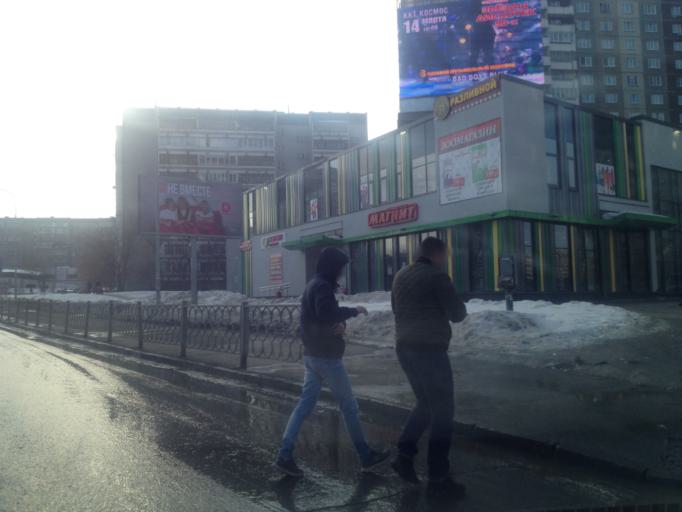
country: RU
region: Sverdlovsk
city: Yekaterinburg
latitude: 56.8535
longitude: 60.5725
